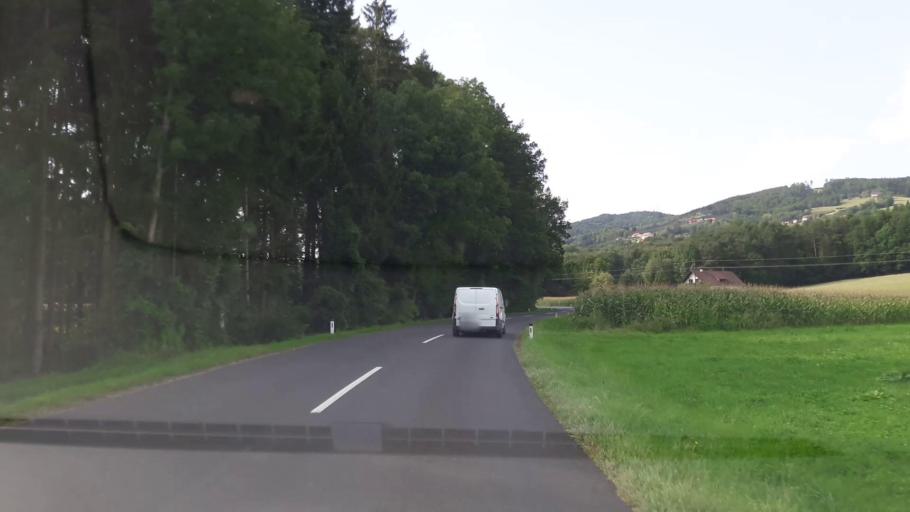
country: AT
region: Styria
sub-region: Politischer Bezirk Hartberg-Fuerstenfeld
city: Kaibing
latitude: 47.2324
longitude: 15.8411
